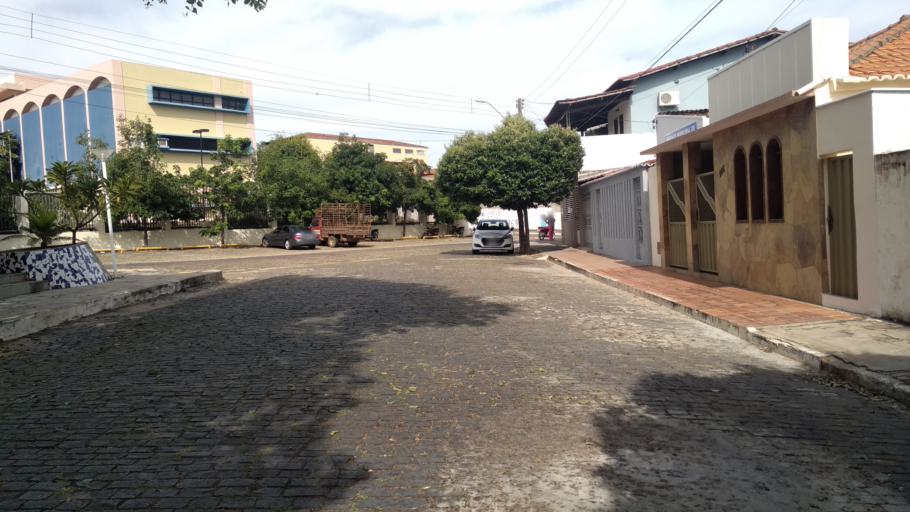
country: BR
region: Bahia
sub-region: Caetite
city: Caetite
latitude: -14.0671
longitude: -42.4932
